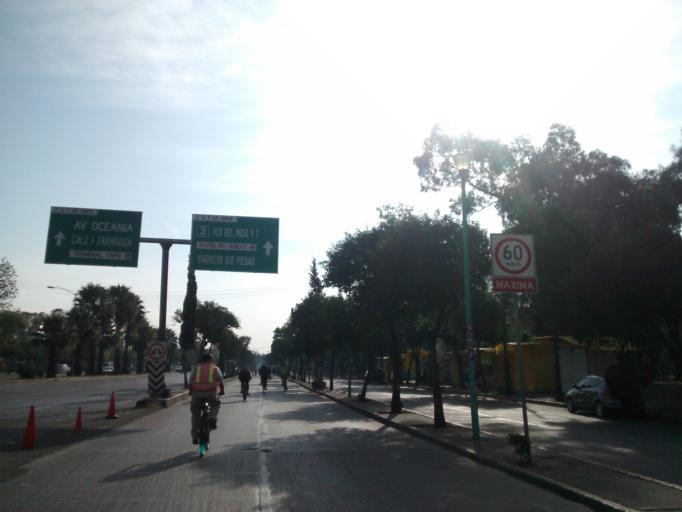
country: MX
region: Mexico City
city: Mexico City
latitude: 19.4219
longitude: -99.1199
